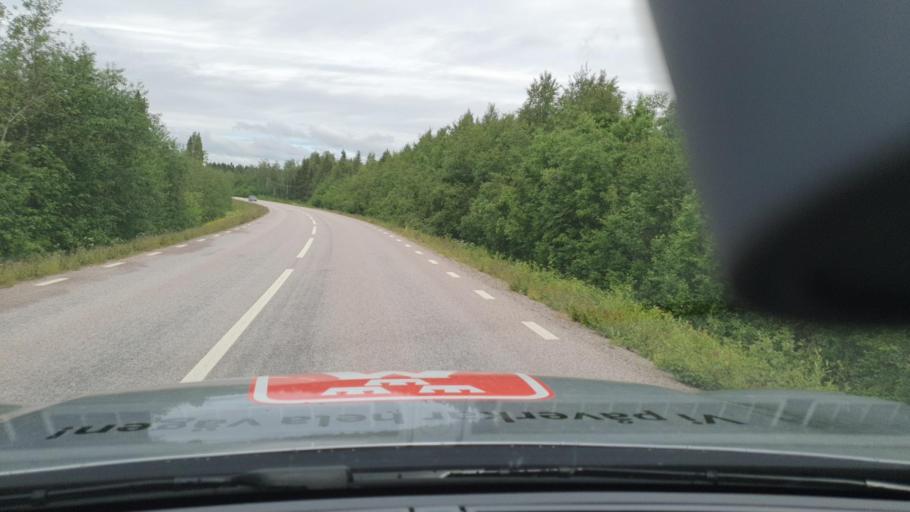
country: SE
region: Norrbotten
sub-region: Lulea Kommun
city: Ranea
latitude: 65.8701
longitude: 22.3005
